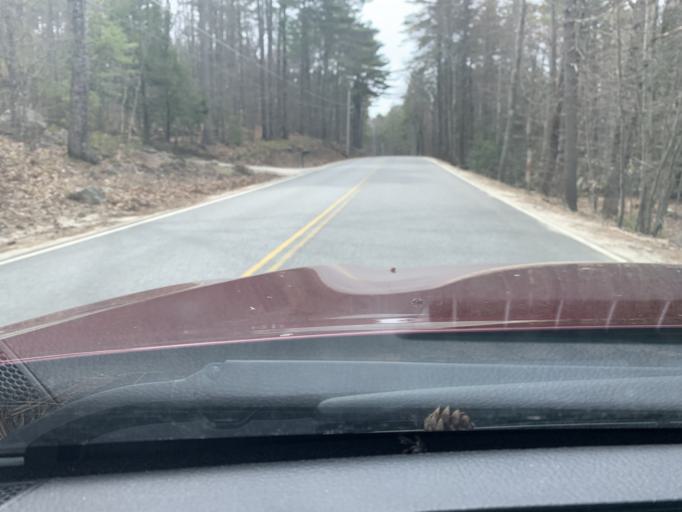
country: US
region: Maine
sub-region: Cumberland County
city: Raymond
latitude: 43.9487
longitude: -70.3863
